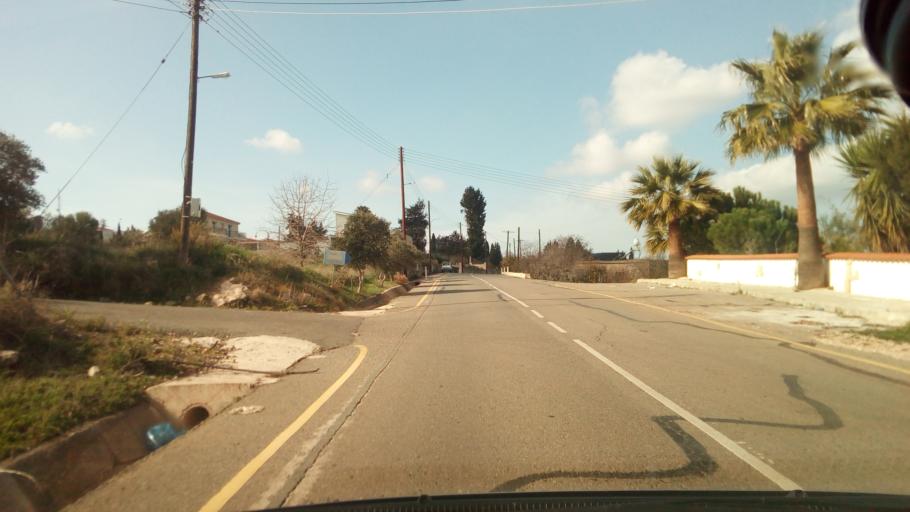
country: CY
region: Pafos
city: Polis
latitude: 34.9620
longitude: 32.4038
